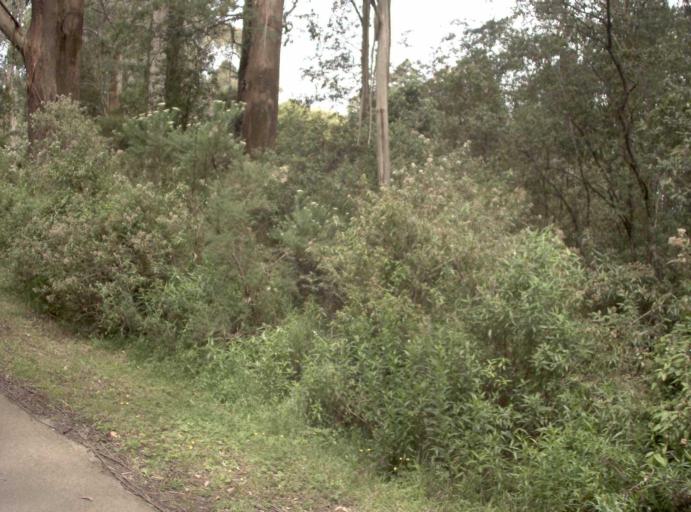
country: AU
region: Victoria
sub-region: Latrobe
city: Traralgon
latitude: -38.4242
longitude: 146.5943
